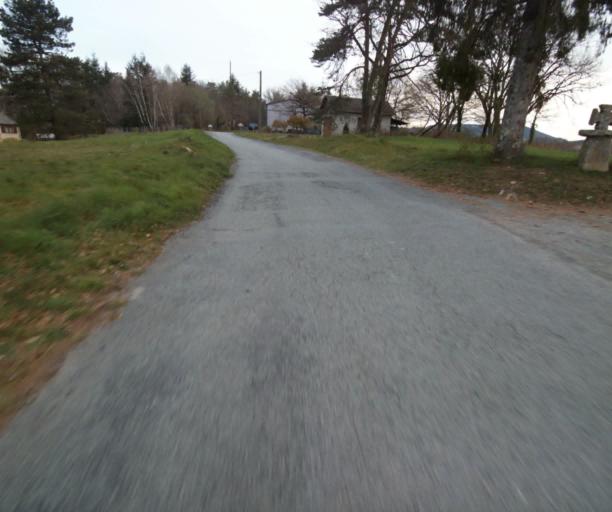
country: FR
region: Limousin
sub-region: Departement de la Correze
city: Correze
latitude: 45.4264
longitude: 1.8363
